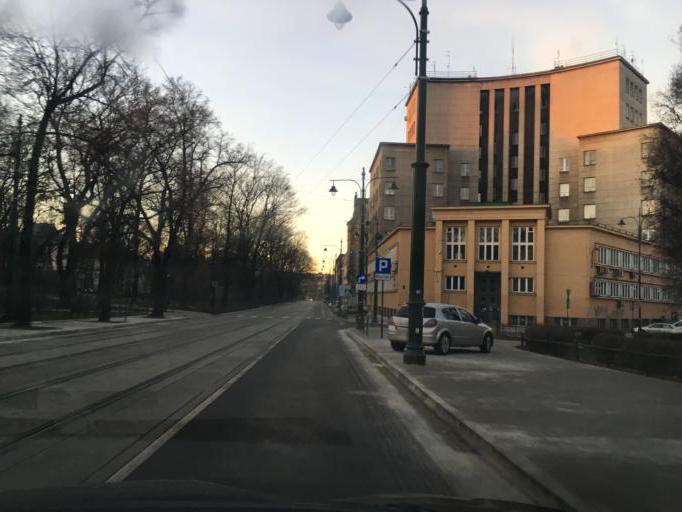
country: PL
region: Lesser Poland Voivodeship
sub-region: Krakow
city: Krakow
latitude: 50.0660
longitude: 19.9358
